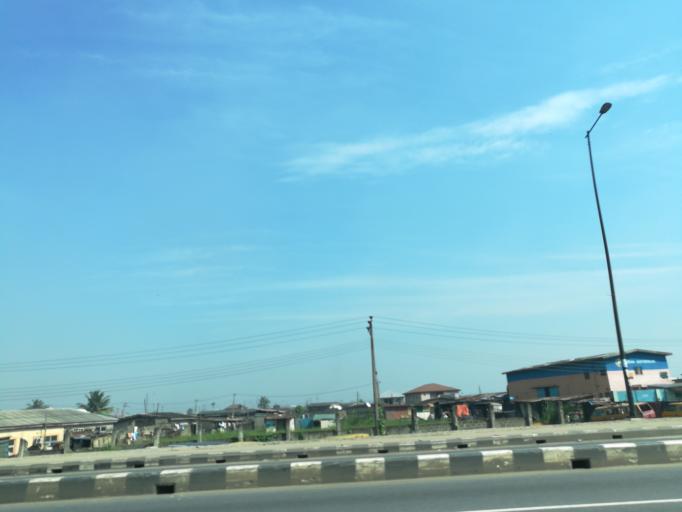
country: NG
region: Lagos
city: Ojota
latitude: 6.6037
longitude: 3.4050
